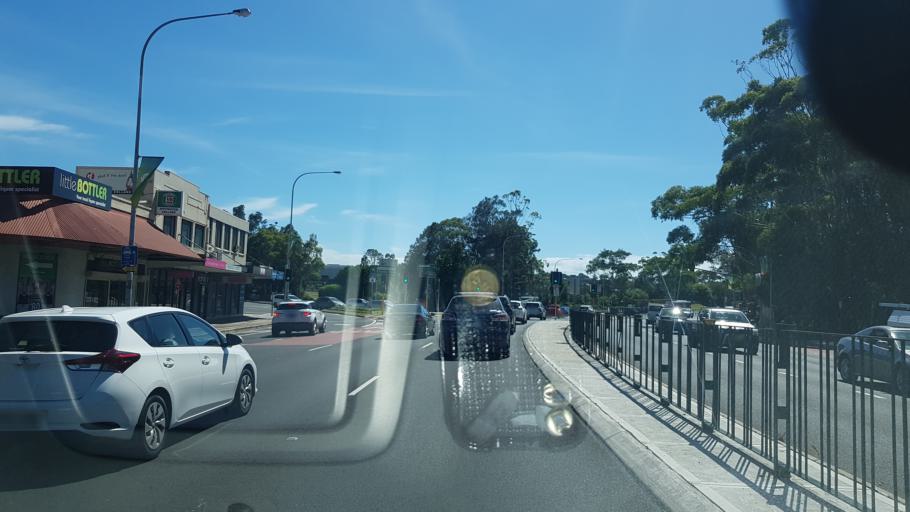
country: AU
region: New South Wales
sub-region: Pittwater
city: Warriewood
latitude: -33.6790
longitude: 151.3034
